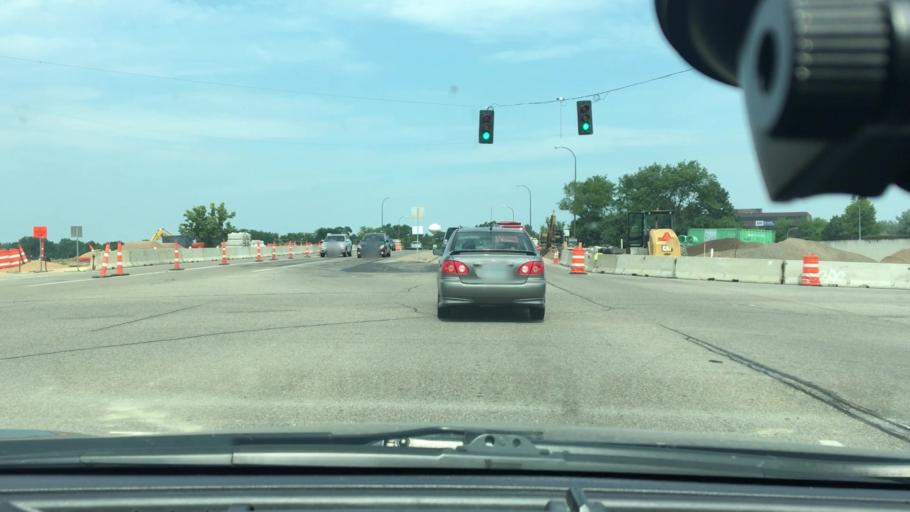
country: US
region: Minnesota
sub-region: Hennepin County
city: Minnetonka Mills
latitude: 44.9694
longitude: -93.4440
